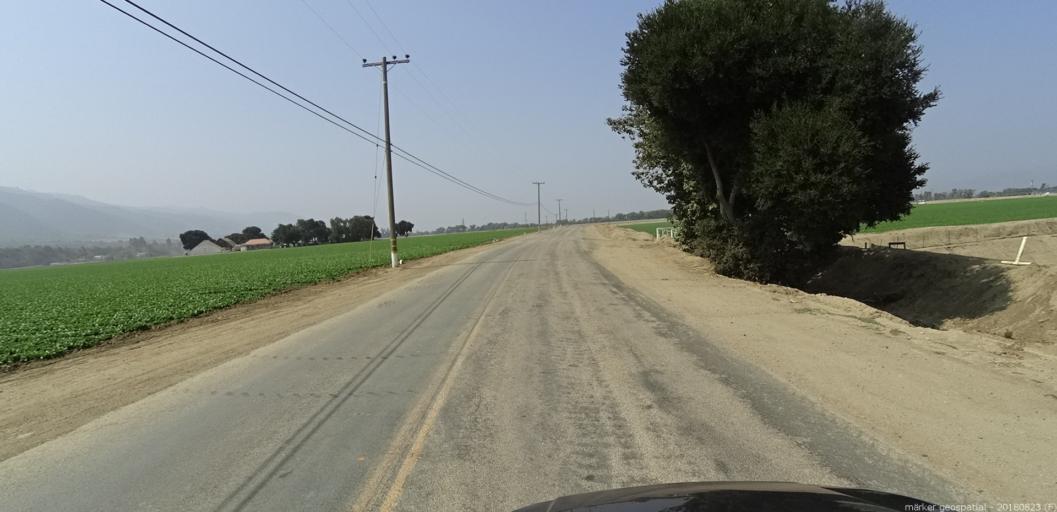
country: US
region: California
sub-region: Monterey County
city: Gonzales
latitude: 36.4770
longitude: -121.4723
